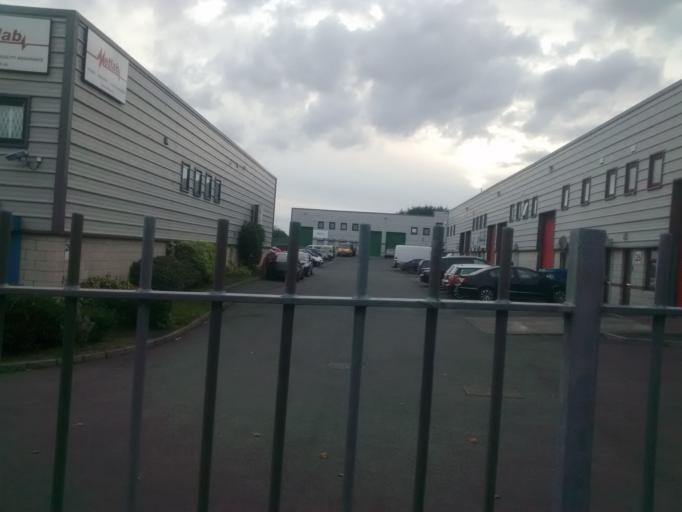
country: IE
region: Leinster
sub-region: Dublin City
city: Finglas
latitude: 53.3791
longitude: -6.2889
